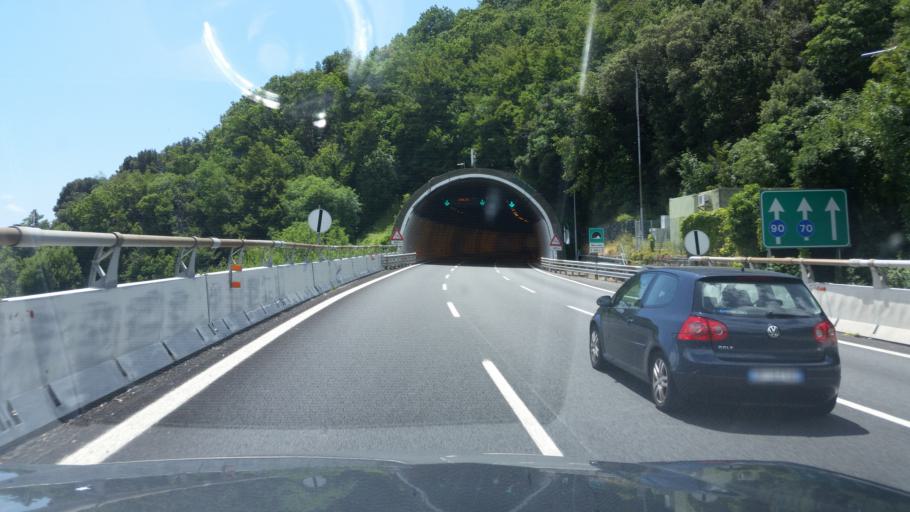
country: IT
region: Liguria
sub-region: Provincia di Genova
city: Mele
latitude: 44.4292
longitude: 8.7405
